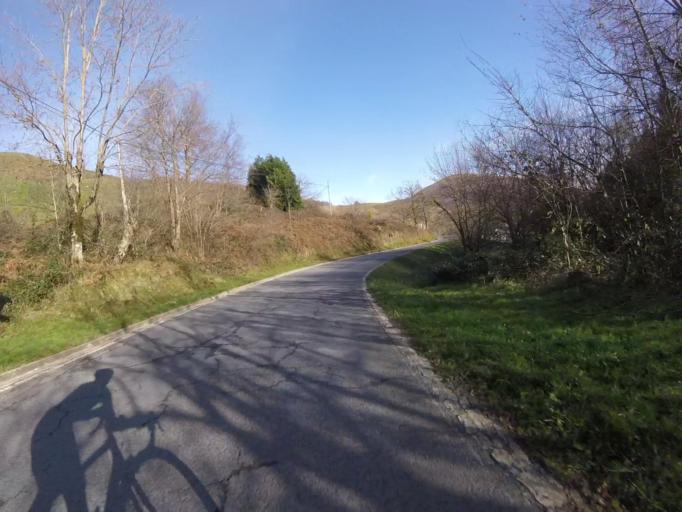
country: ES
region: Navarre
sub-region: Provincia de Navarra
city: Leitza
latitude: 43.0874
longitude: -1.8811
